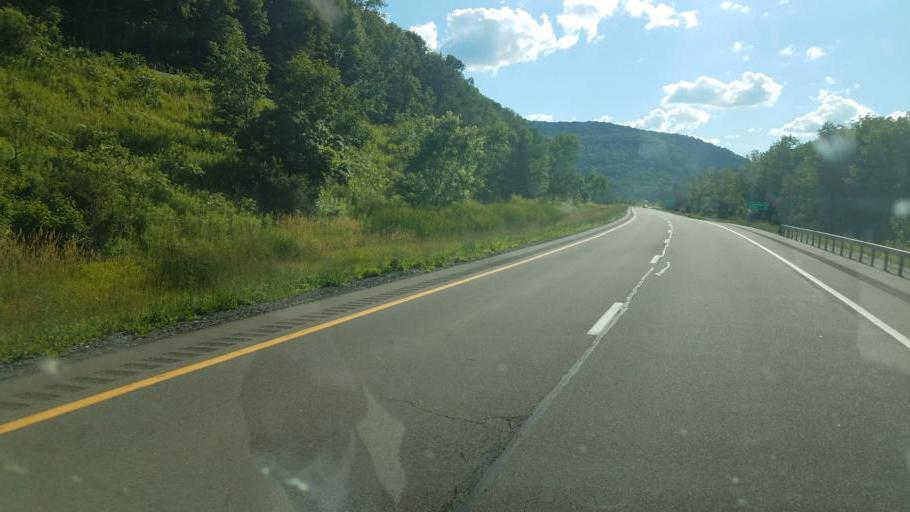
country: US
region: New York
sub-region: Cattaraugus County
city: Salamanca
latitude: 42.1500
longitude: -78.7156
